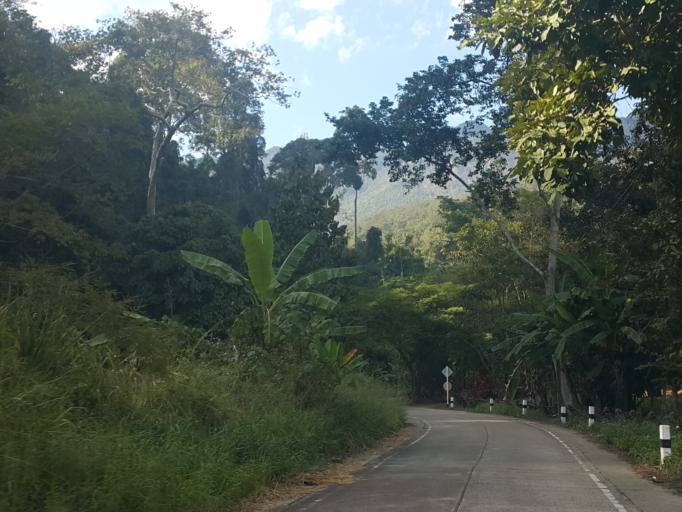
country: TH
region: Chiang Mai
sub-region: Amphoe Chiang Dao
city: Chiang Dao
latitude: 19.4105
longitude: 98.9224
